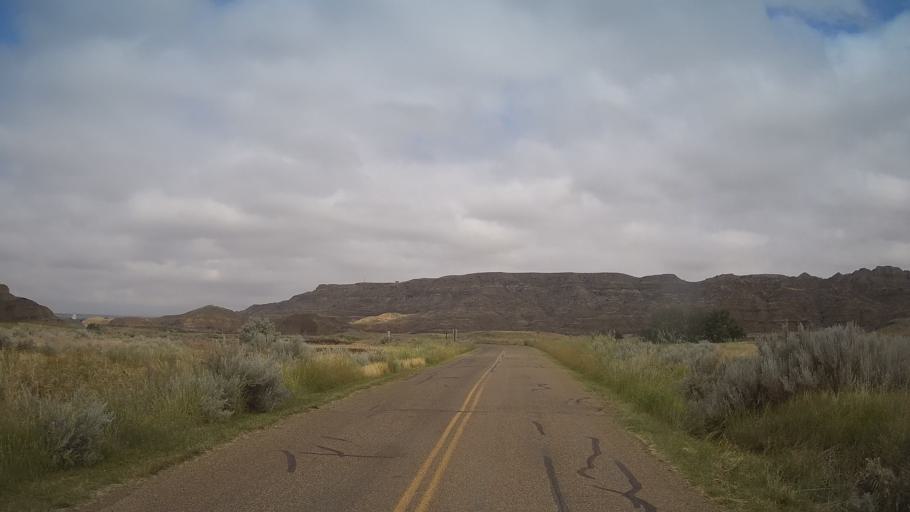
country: US
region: Montana
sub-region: Dawson County
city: Glendive
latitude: 47.0831
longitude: -104.6983
